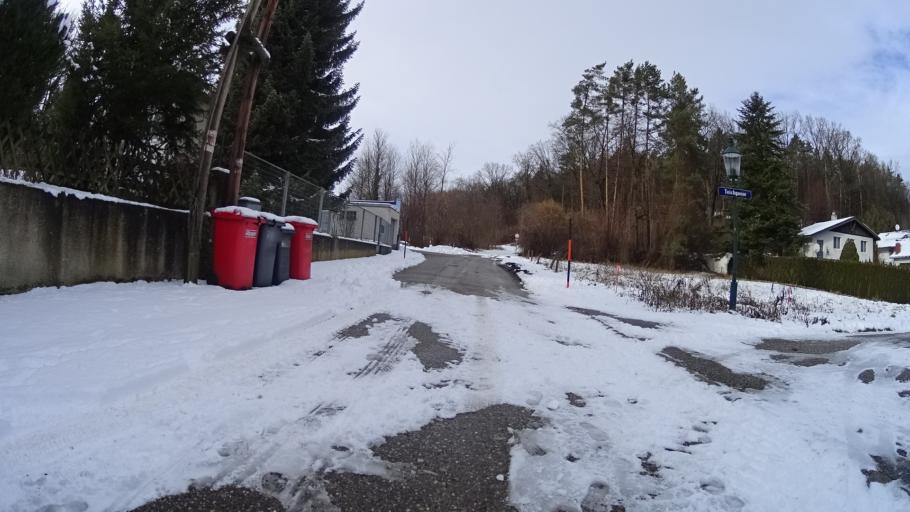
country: AT
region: Lower Austria
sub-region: Politischer Bezirk Korneuburg
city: Niederhollabrunn
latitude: 48.4075
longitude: 16.3035
